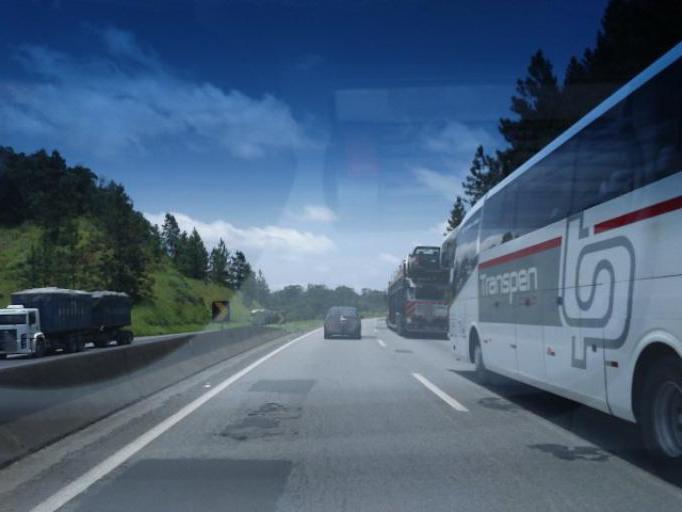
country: BR
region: Sao Paulo
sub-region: Juquia
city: Juquia
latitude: -24.3987
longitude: -47.7322
